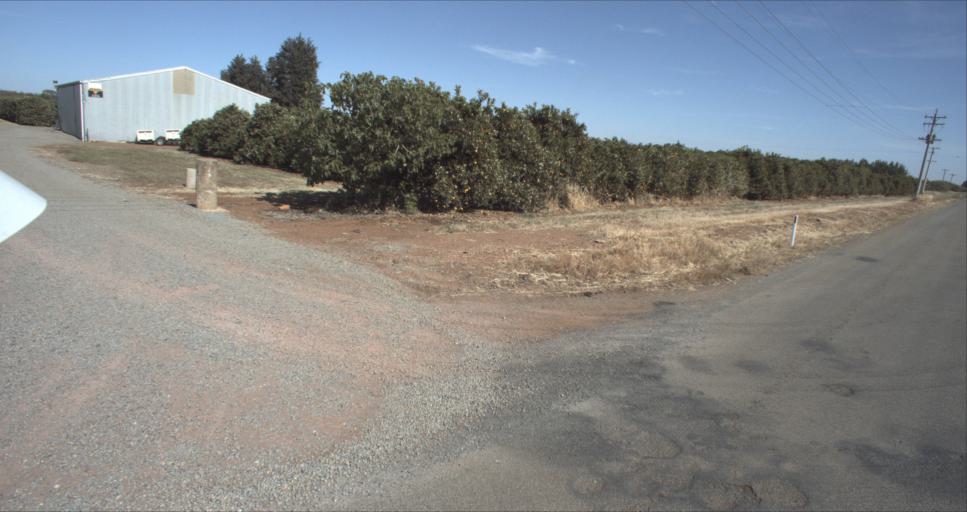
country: AU
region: New South Wales
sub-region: Leeton
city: Leeton
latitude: -34.5741
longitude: 146.4760
